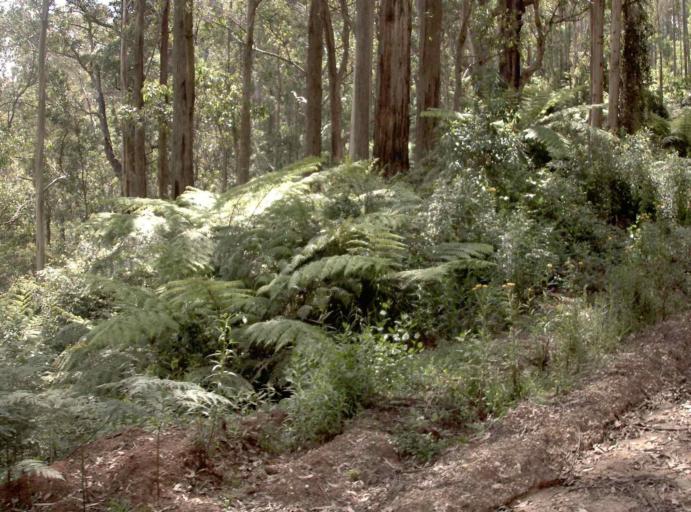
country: AU
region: Victoria
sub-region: East Gippsland
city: Lakes Entrance
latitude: -37.5823
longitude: 148.7263
